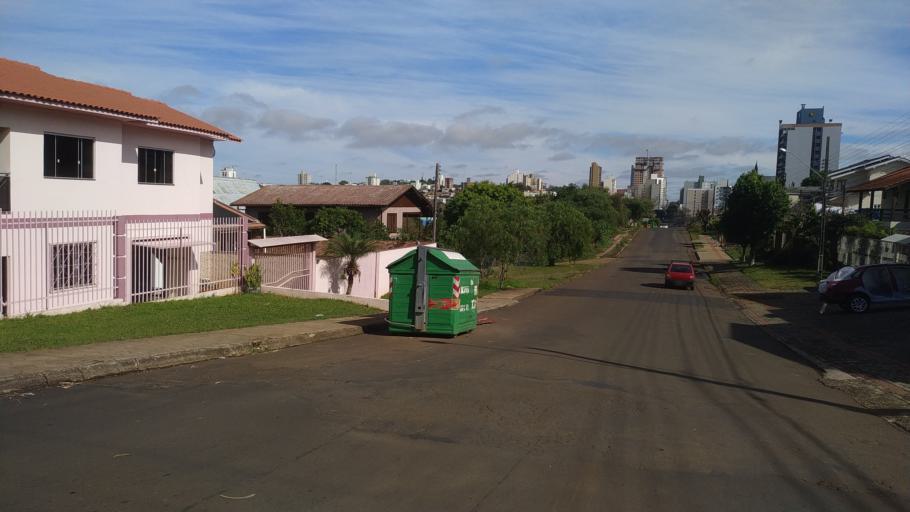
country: BR
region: Santa Catarina
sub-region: Chapeco
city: Chapeco
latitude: -27.1064
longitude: -52.6013
